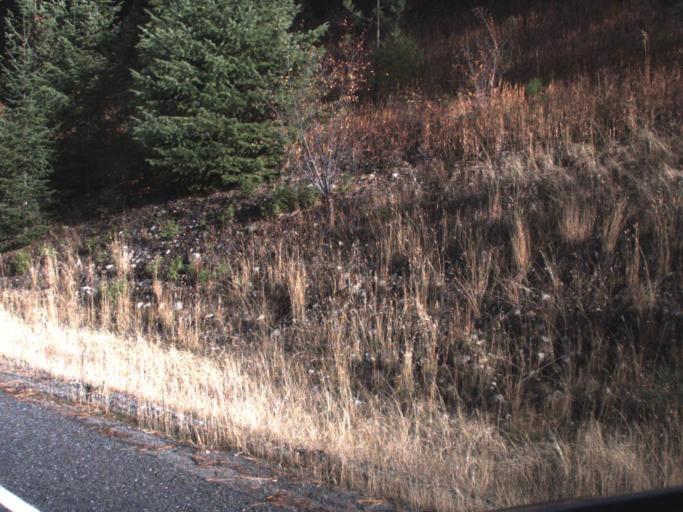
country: US
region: Washington
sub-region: Stevens County
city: Kettle Falls
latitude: 48.6755
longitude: -118.0220
